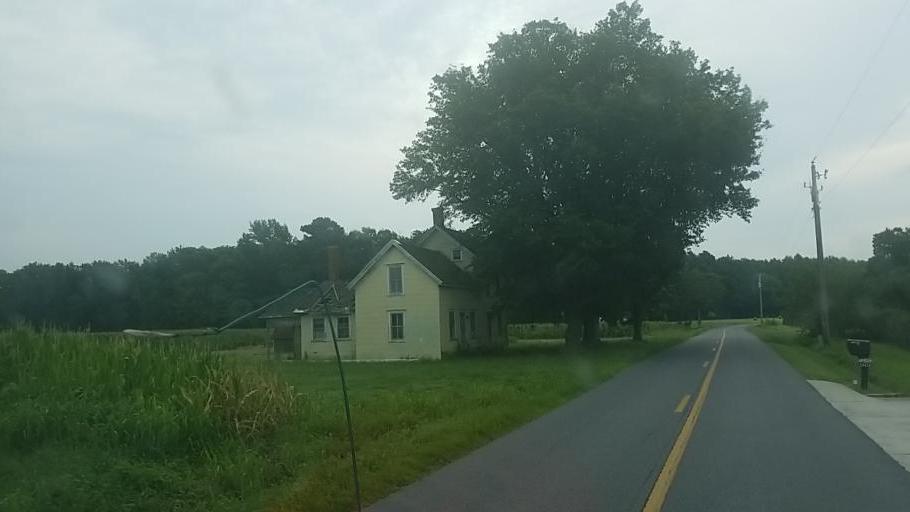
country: US
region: Delaware
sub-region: Sussex County
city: Selbyville
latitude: 38.4438
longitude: -75.2039
